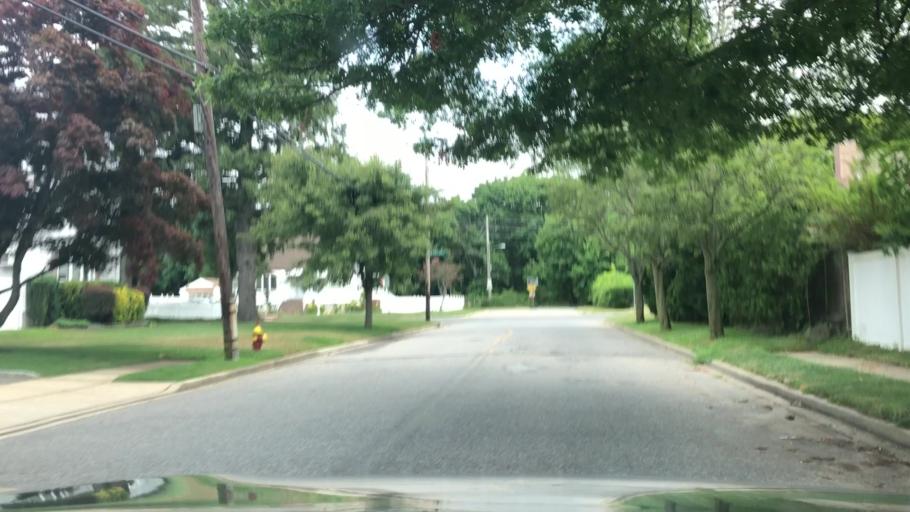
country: US
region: New York
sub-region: Nassau County
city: North Massapequa
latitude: 40.7042
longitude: -73.4678
